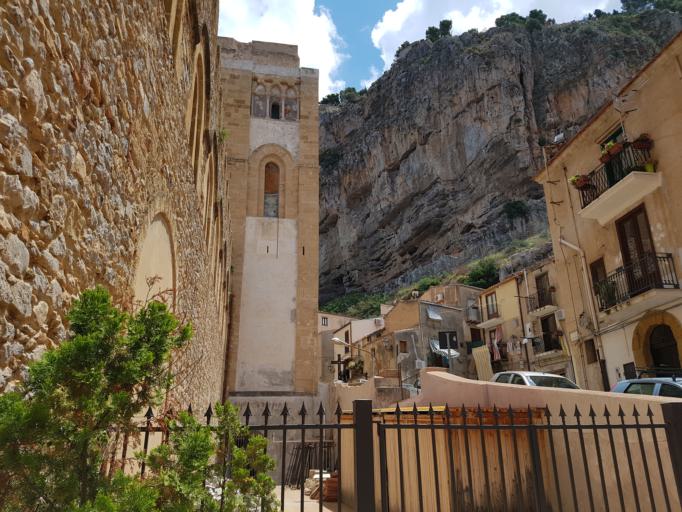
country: IT
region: Sicily
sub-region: Palermo
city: Cefalu
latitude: 38.0397
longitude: 14.0233
